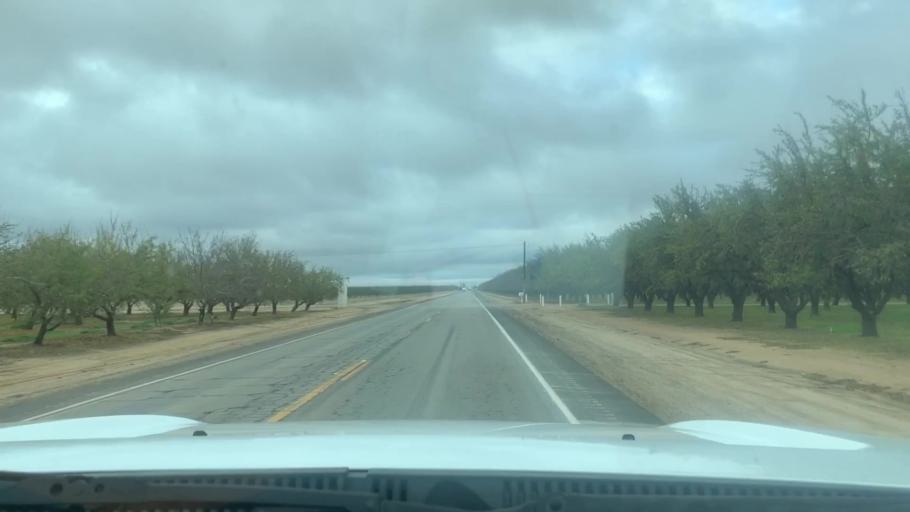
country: US
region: California
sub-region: Kern County
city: Rosedale
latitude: 35.4771
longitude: -119.1532
